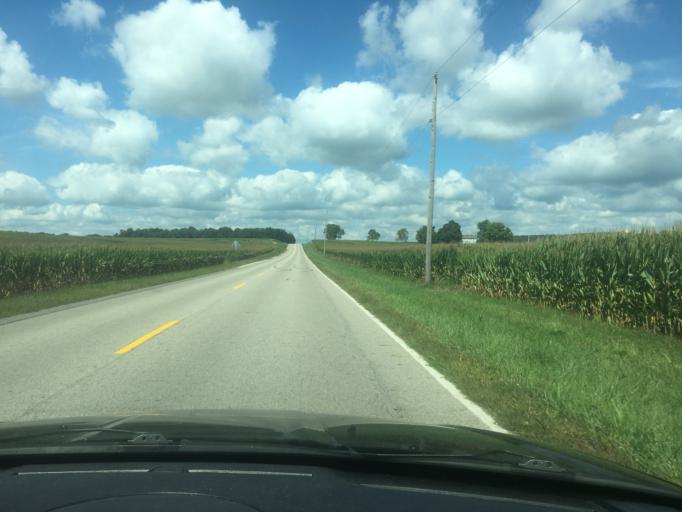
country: US
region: Ohio
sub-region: Logan County
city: West Liberty
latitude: 40.2304
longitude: -83.7083
